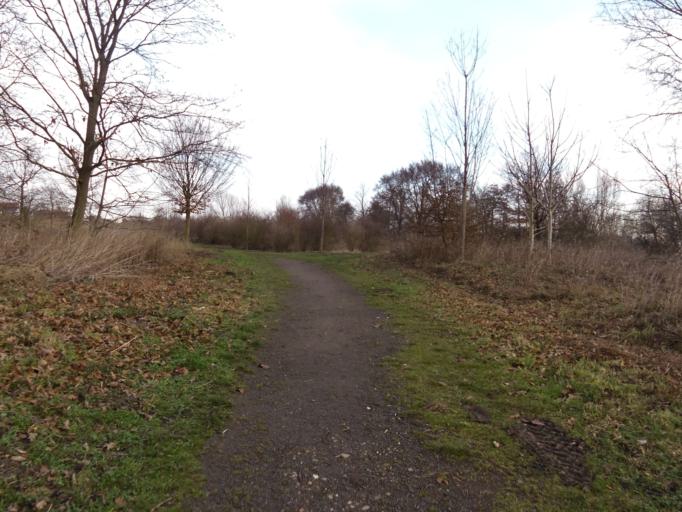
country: DE
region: Rheinland-Pfalz
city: Bobenheim-Roxheim
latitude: 49.5661
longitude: 8.3558
